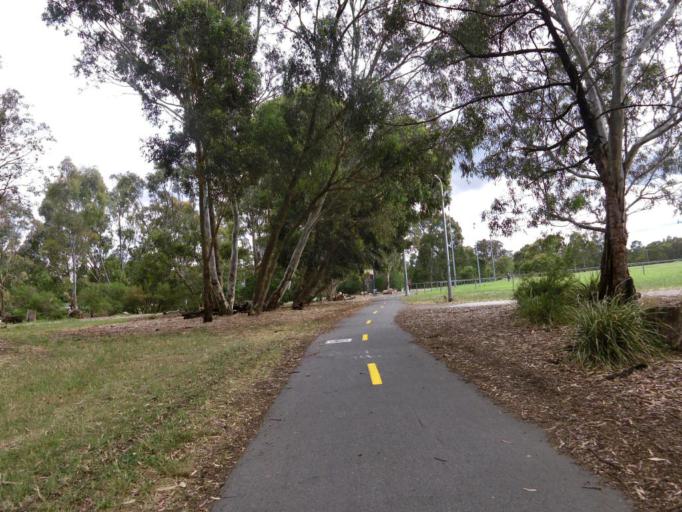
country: AU
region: Victoria
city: Heidelberg West
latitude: -37.7381
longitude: 145.0329
